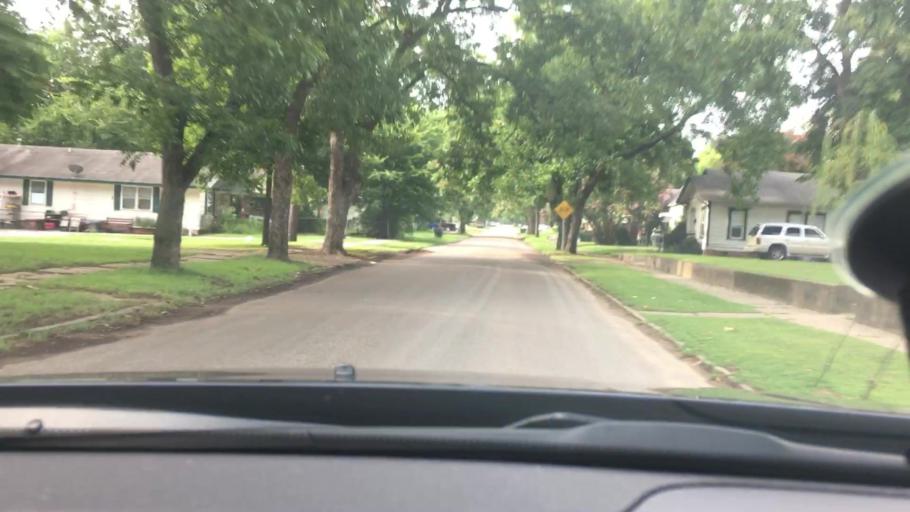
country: US
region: Oklahoma
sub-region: Carter County
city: Ardmore
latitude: 34.1824
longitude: -97.1280
